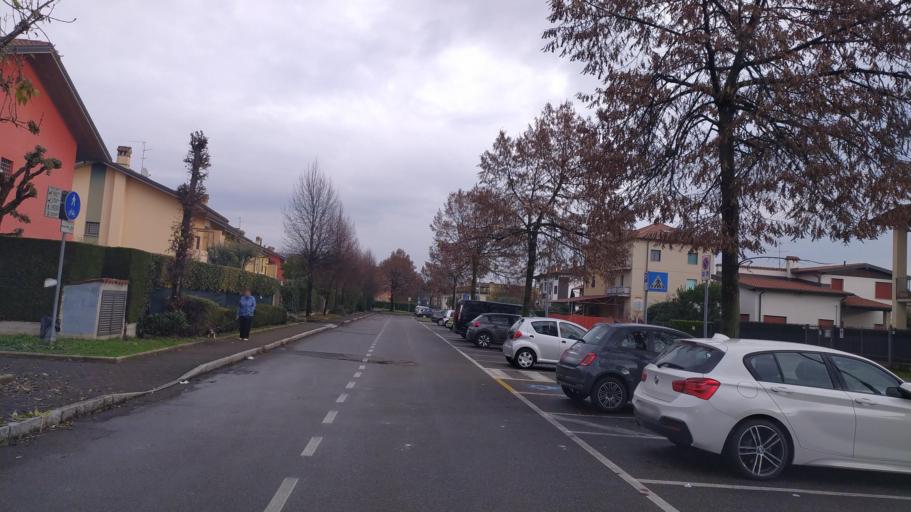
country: IT
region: Lombardy
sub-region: Provincia di Bergamo
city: Treviolo
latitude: 45.6749
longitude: 9.6221
